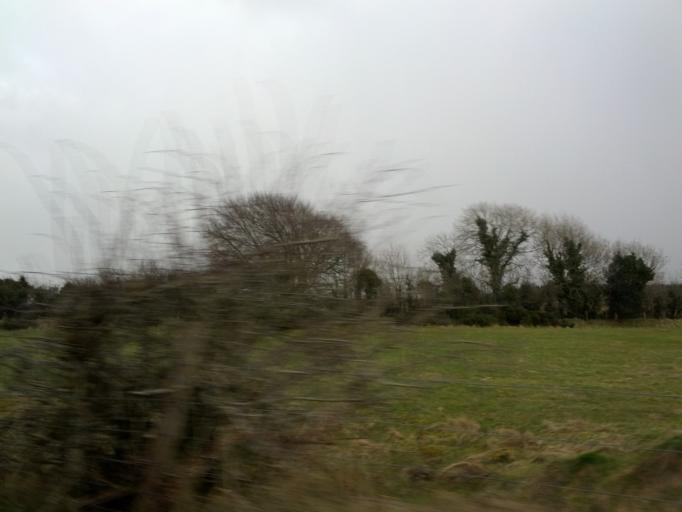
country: IE
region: Connaught
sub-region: County Galway
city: Athenry
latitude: 53.4000
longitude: -8.6104
